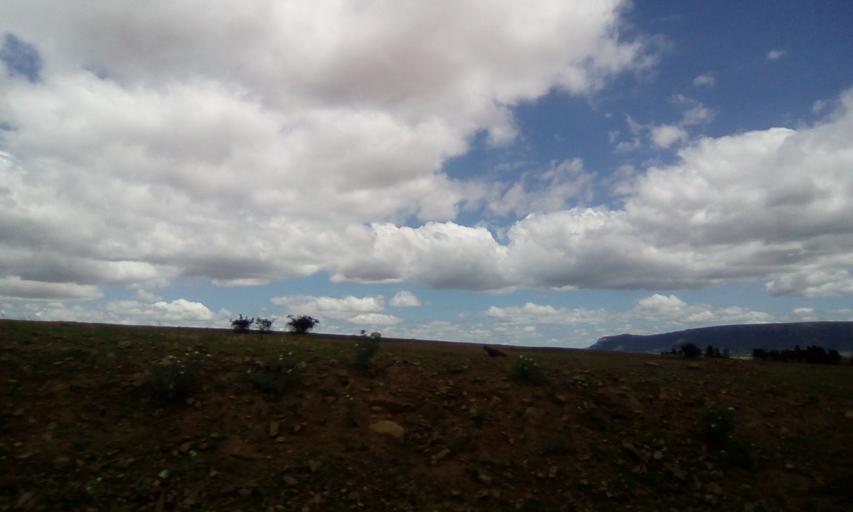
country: LS
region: Maseru
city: Maseru
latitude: -29.3940
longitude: 27.6328
